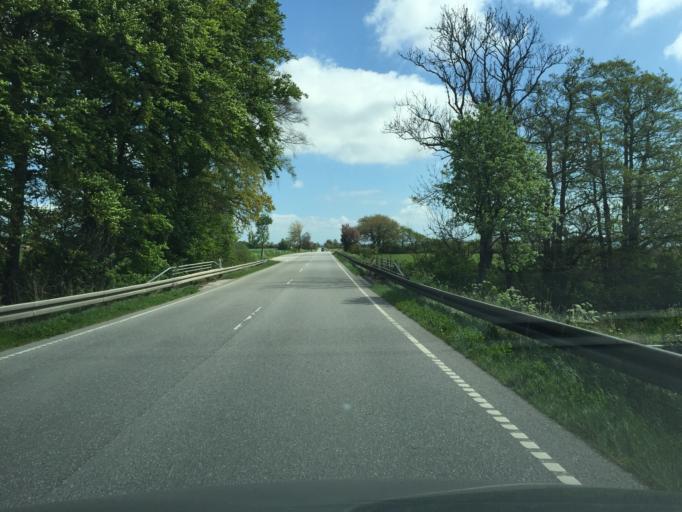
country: DK
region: Zealand
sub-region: Guldborgsund Kommune
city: Stubbekobing
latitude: 54.9977
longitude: 12.1091
